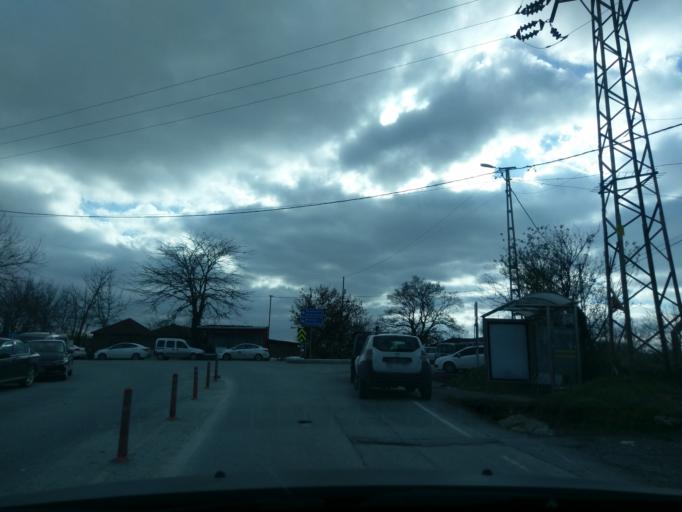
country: TR
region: Istanbul
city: Boyalik
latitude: 41.2739
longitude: 28.6613
